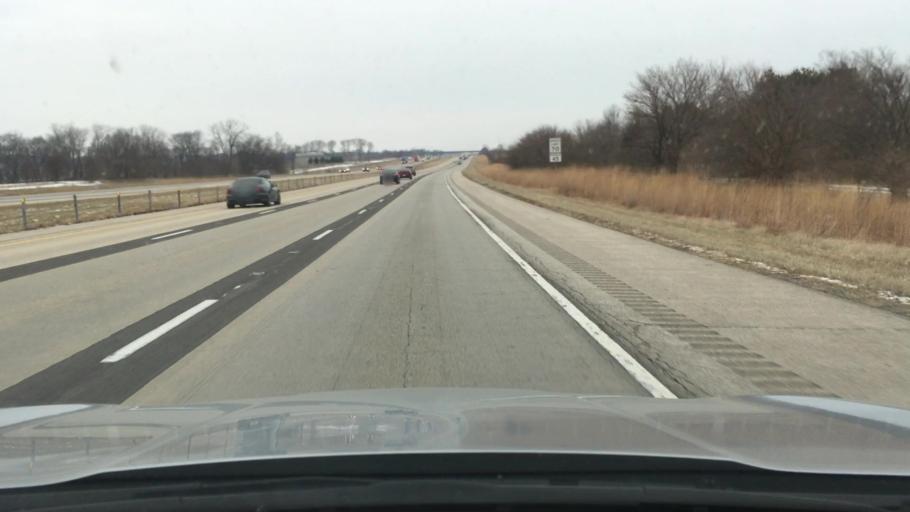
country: US
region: Illinois
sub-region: Sangamon County
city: Divernon
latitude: 39.6353
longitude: -89.6469
